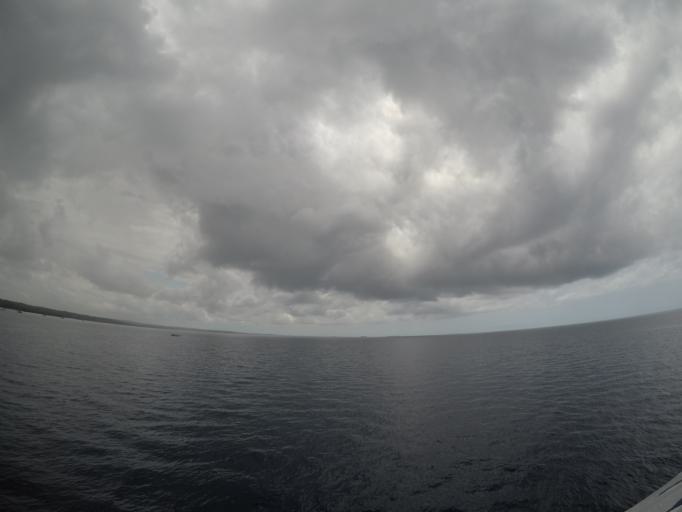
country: TZ
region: Zanzibar North
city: Mkokotoni
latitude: -5.9974
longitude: 39.1758
